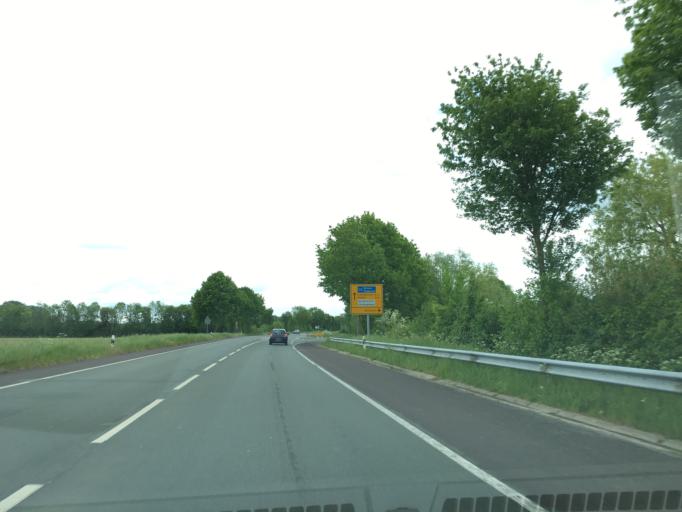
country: DE
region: North Rhine-Westphalia
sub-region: Regierungsbezirk Munster
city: Senden
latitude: 51.9222
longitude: 7.4716
